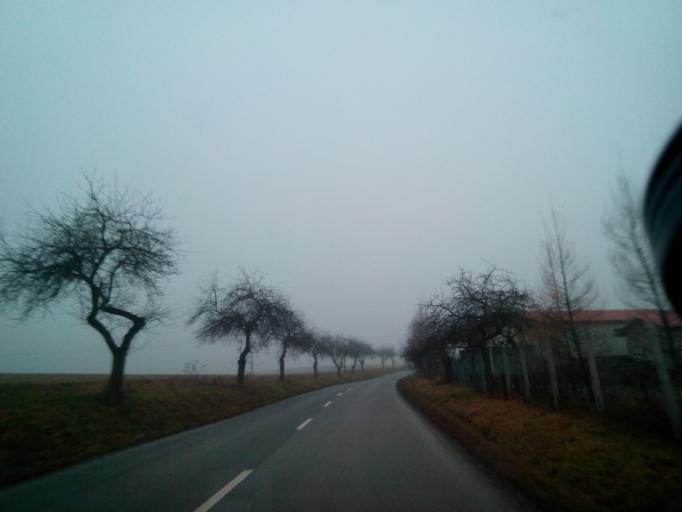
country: SK
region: Kosicky
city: Krompachy
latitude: 48.9812
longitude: 20.9441
